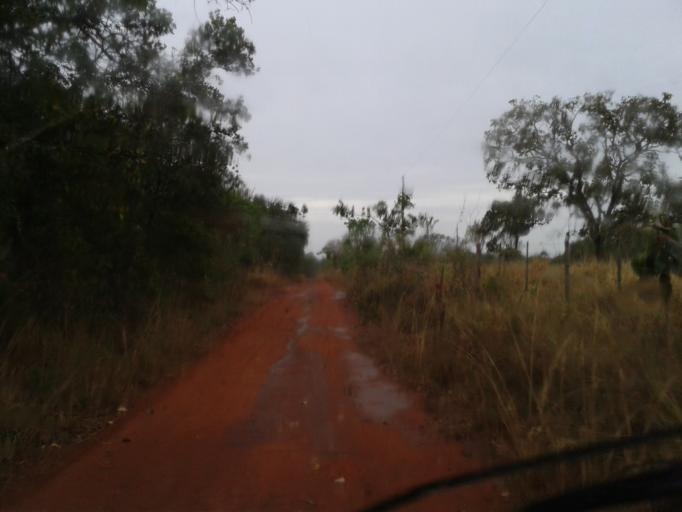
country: BR
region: Minas Gerais
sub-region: Campina Verde
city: Campina Verde
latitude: -19.3395
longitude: -49.5216
